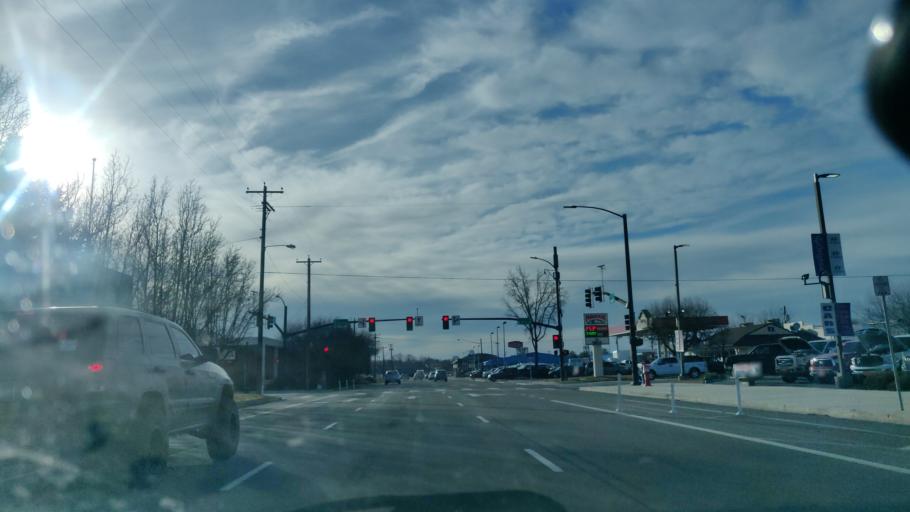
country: US
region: Idaho
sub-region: Ada County
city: Garden City
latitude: 43.6218
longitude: -116.2233
